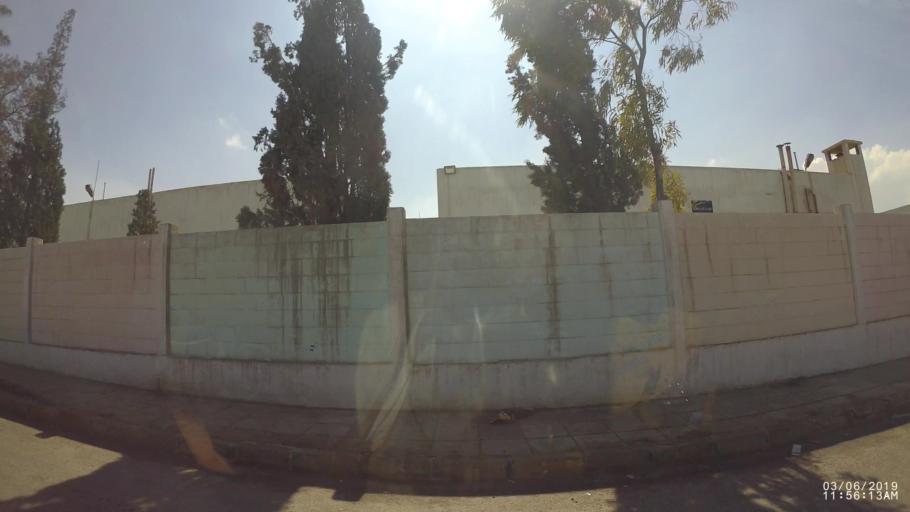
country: JO
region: Zarqa
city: Russeifa
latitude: 31.9841
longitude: 36.0144
